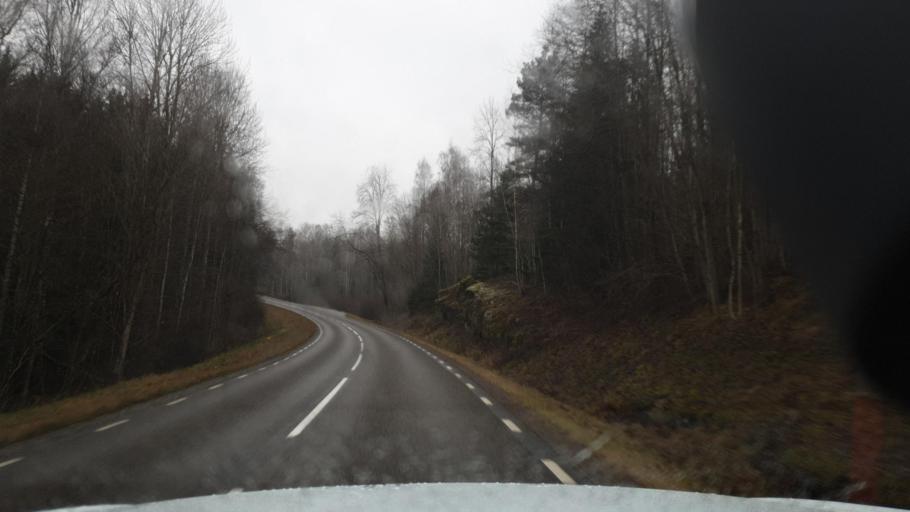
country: SE
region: Vaermland
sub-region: Eda Kommun
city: Amotfors
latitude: 59.7205
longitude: 12.4276
